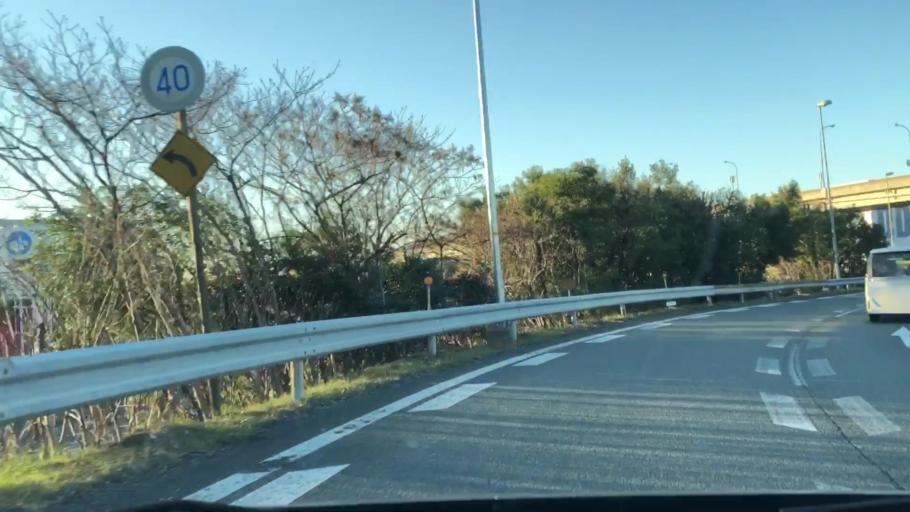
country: JP
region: Fukuoka
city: Umi
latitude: 33.6285
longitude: 130.4830
